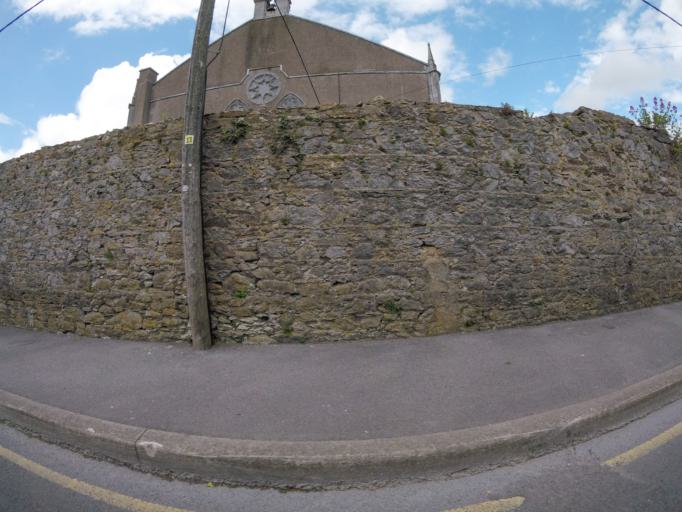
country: IE
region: Munster
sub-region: Waterford
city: Dungarvan
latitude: 52.0873
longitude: -7.6208
